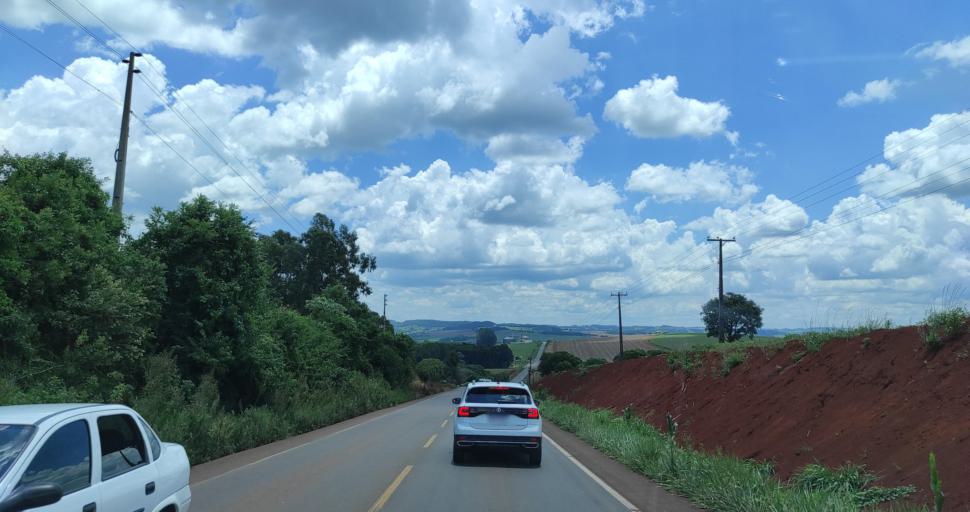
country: BR
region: Santa Catarina
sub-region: Xanxere
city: Xanxere
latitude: -26.7766
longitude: -52.4068
